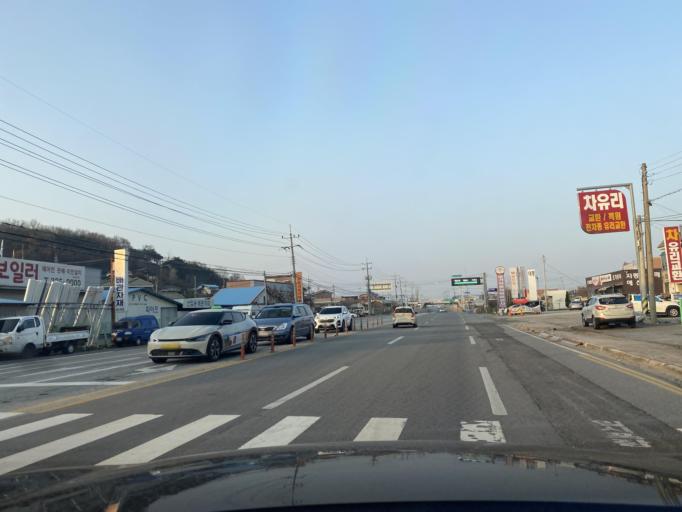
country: KR
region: Chungcheongnam-do
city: Yesan
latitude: 36.6911
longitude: 126.8280
